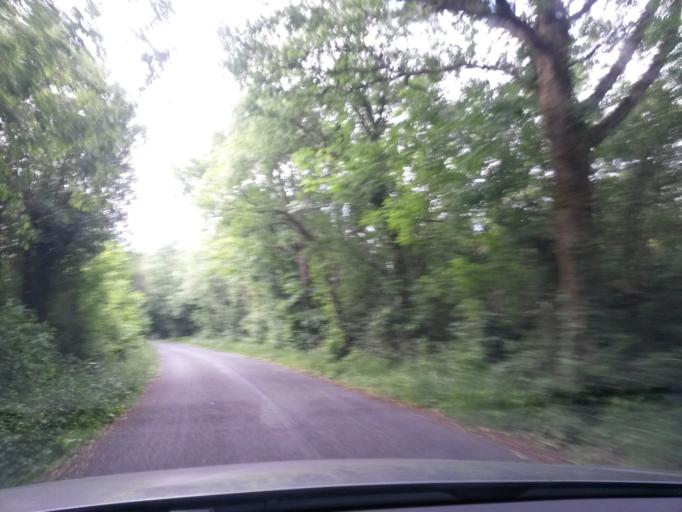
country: IE
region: Connaught
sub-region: Sligo
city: Sligo
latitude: 54.2427
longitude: -8.4441
